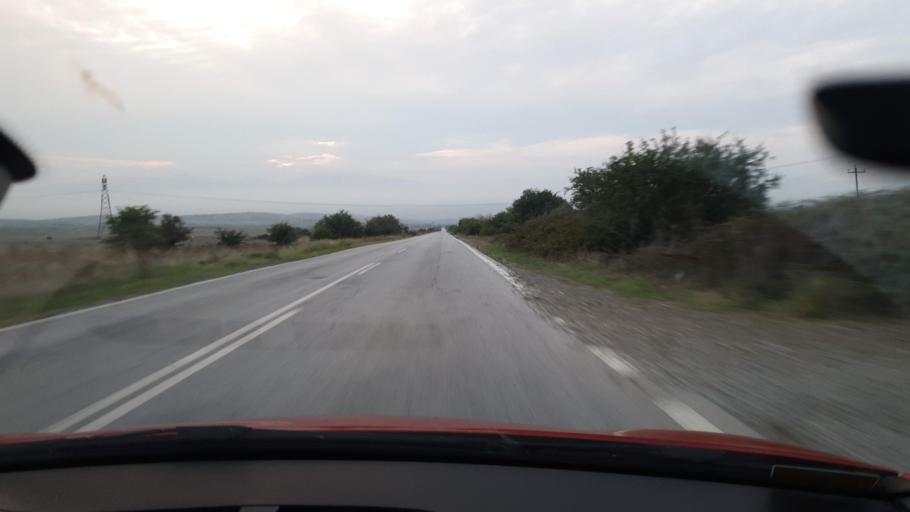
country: GR
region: Central Macedonia
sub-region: Nomos Kilkis
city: Polykastro
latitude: 41.0054
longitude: 22.7102
